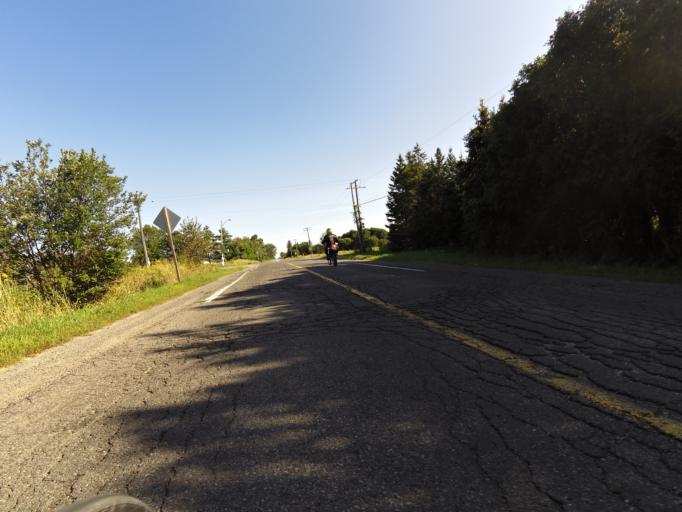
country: CA
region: Ontario
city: Bells Corners
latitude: 45.4671
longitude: -76.0077
